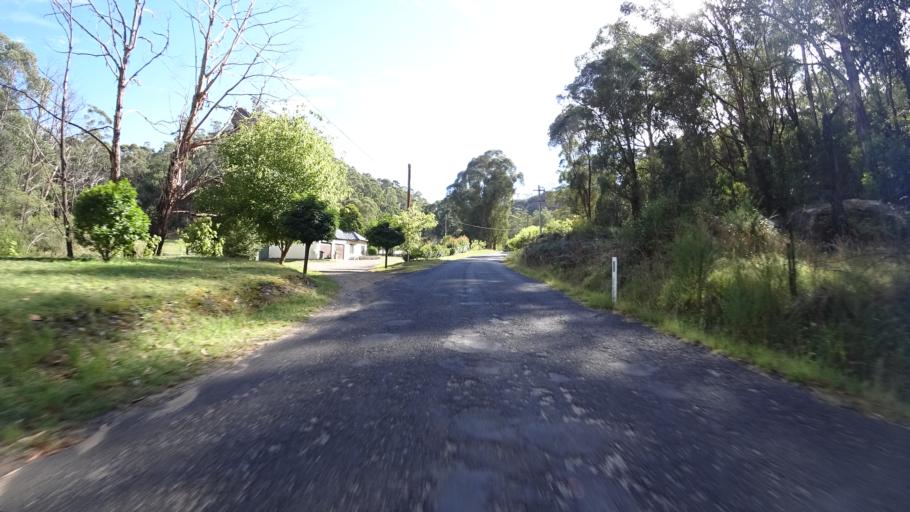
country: AU
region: New South Wales
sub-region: Lithgow
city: Lithgow
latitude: -33.4566
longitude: 150.1722
